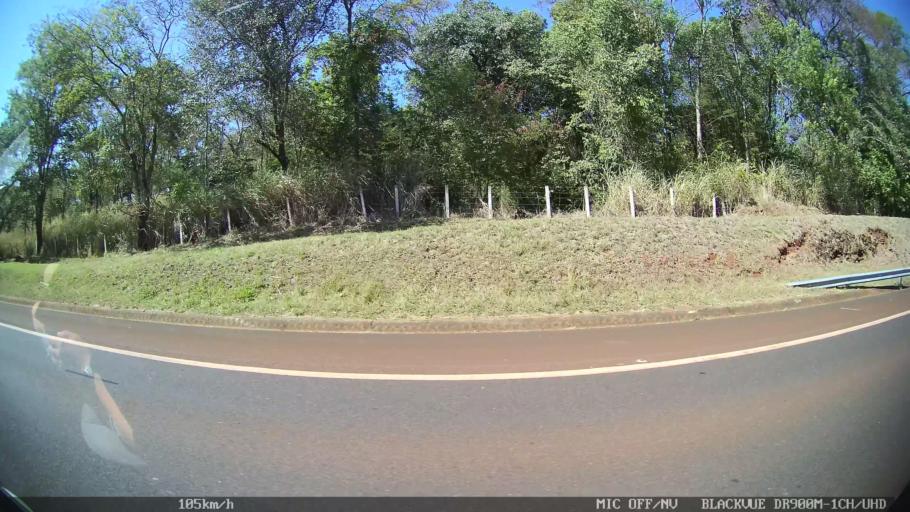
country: BR
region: Sao Paulo
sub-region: Franca
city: Franca
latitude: -20.6209
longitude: -47.4596
